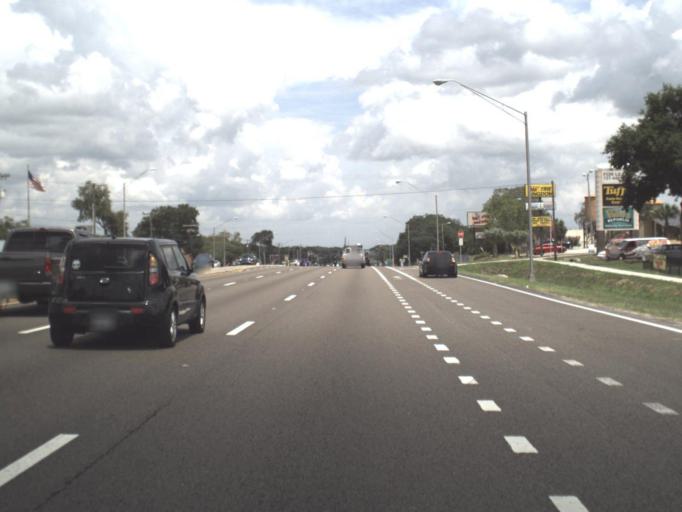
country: US
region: Florida
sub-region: Hillsborough County
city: Temple Terrace
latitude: 28.0543
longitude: -82.3996
